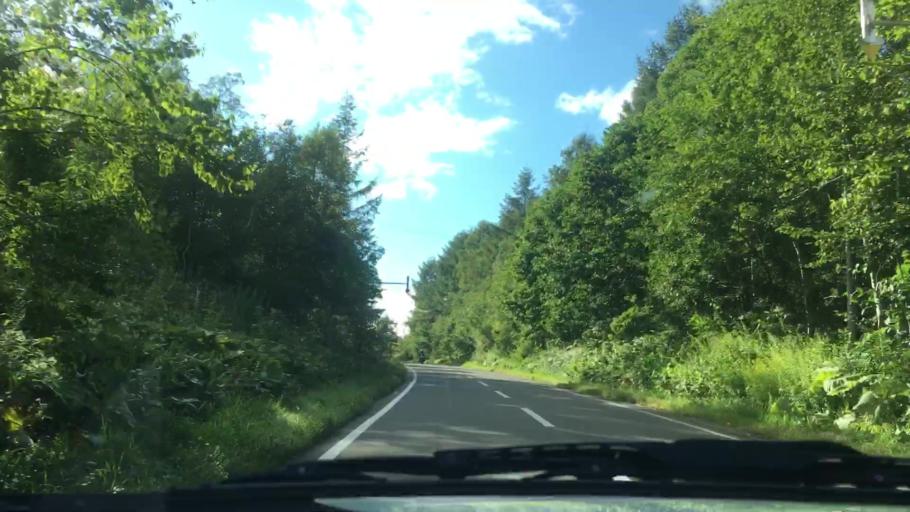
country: JP
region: Hokkaido
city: Otofuke
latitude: 43.1727
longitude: 142.9725
